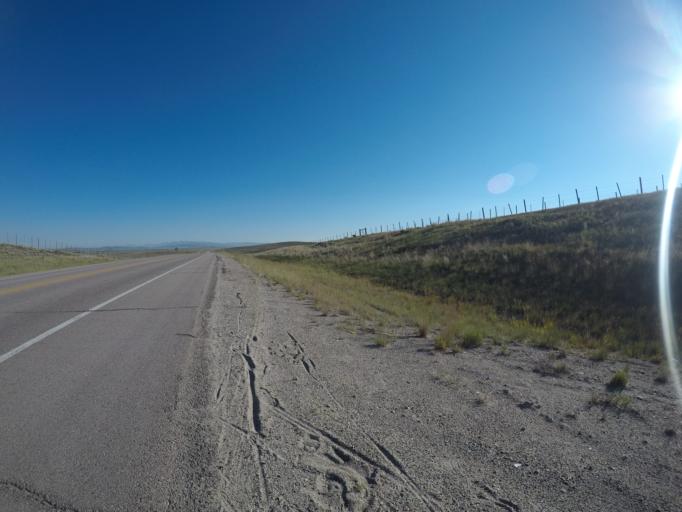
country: US
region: Wyoming
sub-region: Sublette County
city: Pinedale
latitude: 42.9139
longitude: -110.0784
